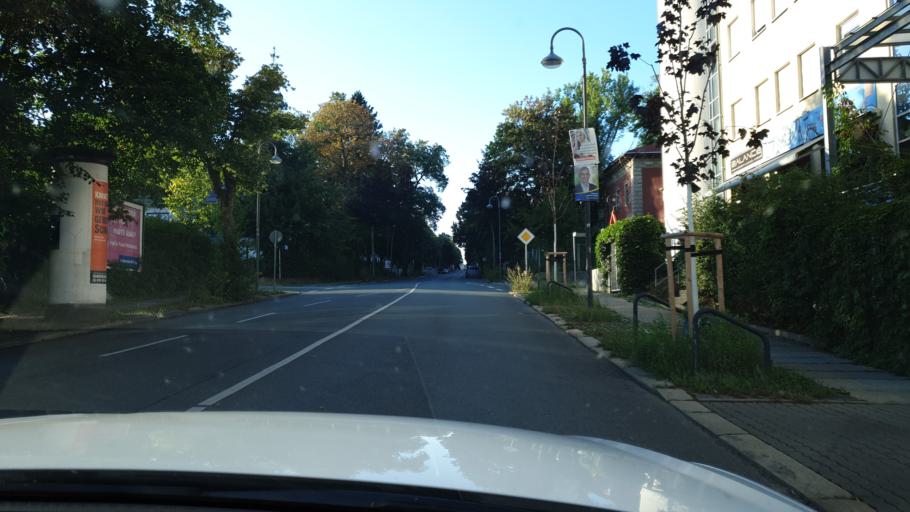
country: DE
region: Saxony
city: Chemnitz
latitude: 50.8267
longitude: 12.9045
